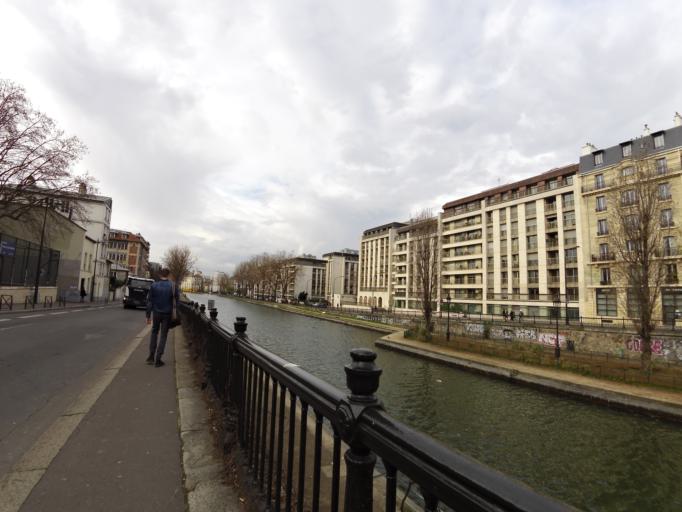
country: FR
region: Ile-de-France
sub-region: Paris
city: Paris
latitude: 48.8772
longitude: 2.3656
